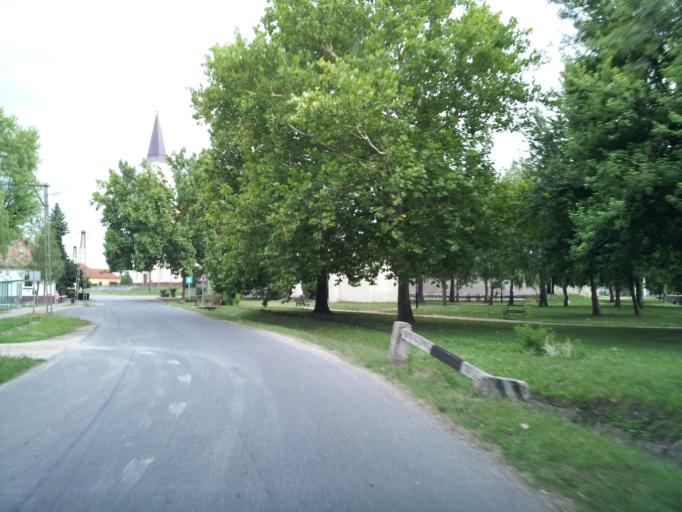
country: HU
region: Veszprem
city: Devecser
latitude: 47.1205
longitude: 17.3770
